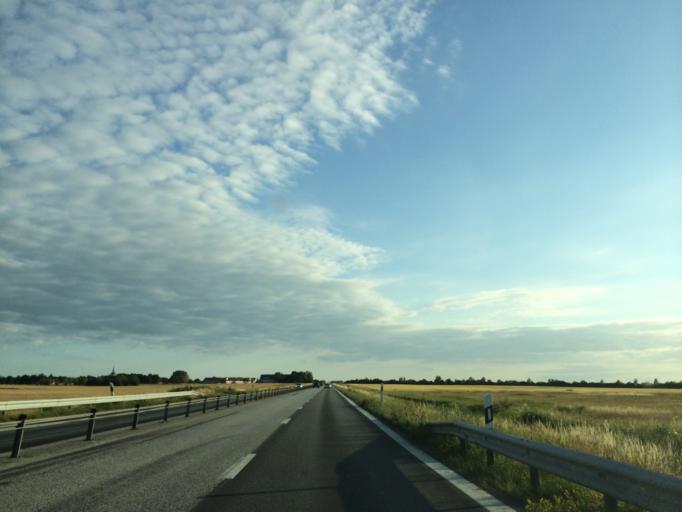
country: SE
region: Skane
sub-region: Vellinge Kommun
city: Hollviken
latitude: 55.4329
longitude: 12.9760
